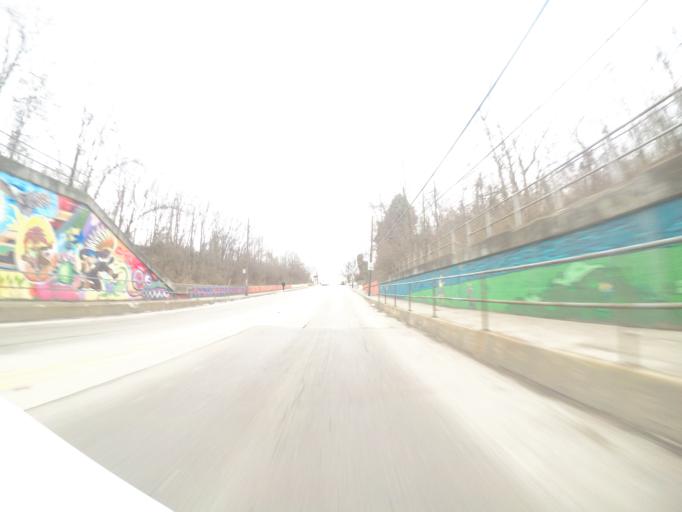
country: US
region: Ohio
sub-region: Lucas County
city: Oregon
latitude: 41.6248
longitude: -83.5154
